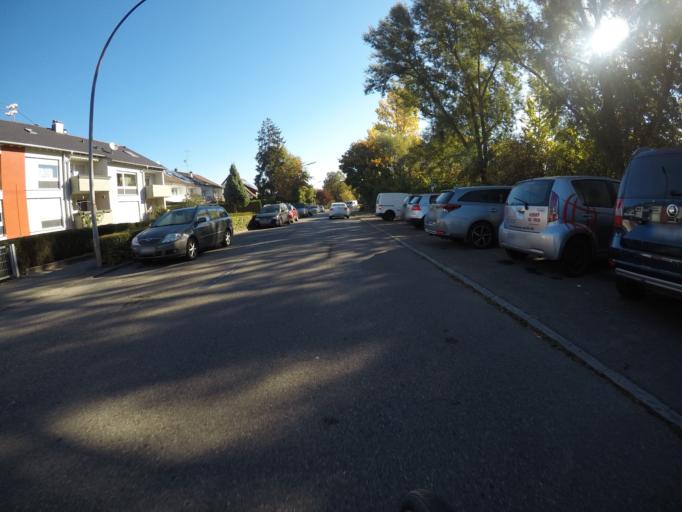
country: DE
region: Baden-Wuerttemberg
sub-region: Regierungsbezirk Stuttgart
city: Filderstadt
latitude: 48.6738
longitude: 9.2127
